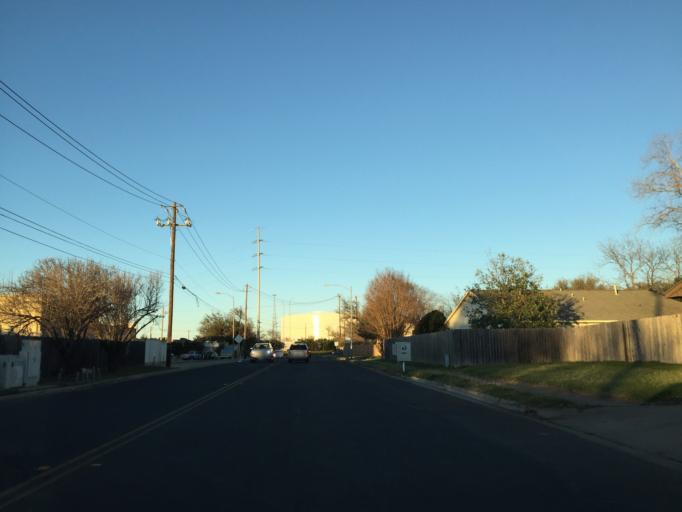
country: US
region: Texas
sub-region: Williamson County
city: Jollyville
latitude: 30.4322
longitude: -97.7697
